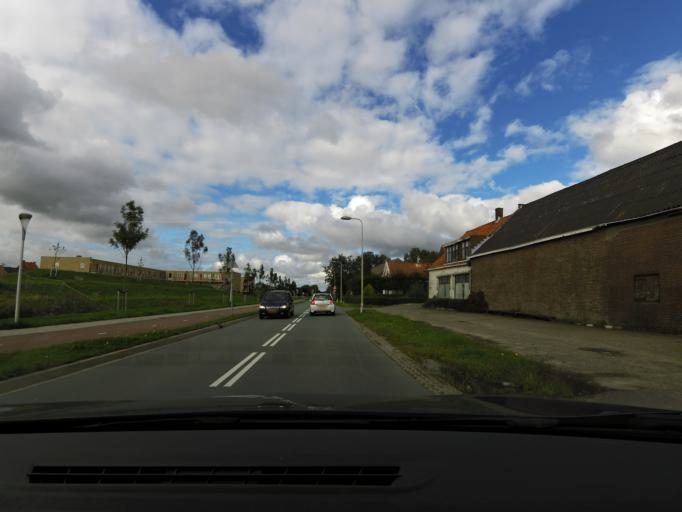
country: NL
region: South Holland
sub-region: Gemeente Brielle
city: Brielle
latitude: 51.8913
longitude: 4.1807
